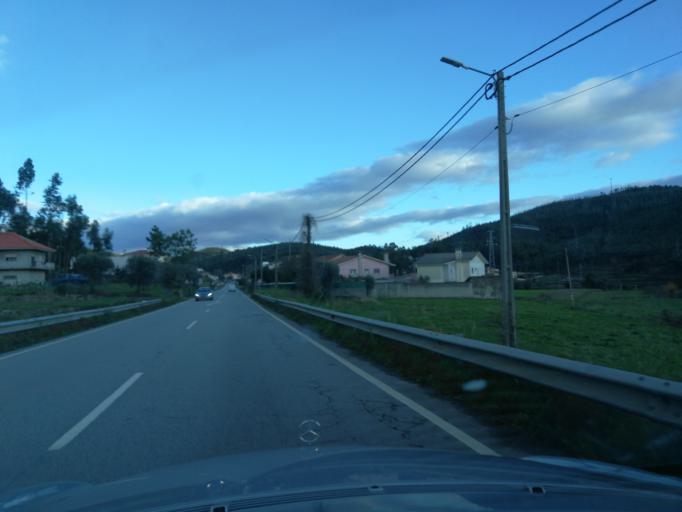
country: PT
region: Braga
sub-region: Barcelos
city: Vila Frescainha
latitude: 41.5725
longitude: -8.6949
